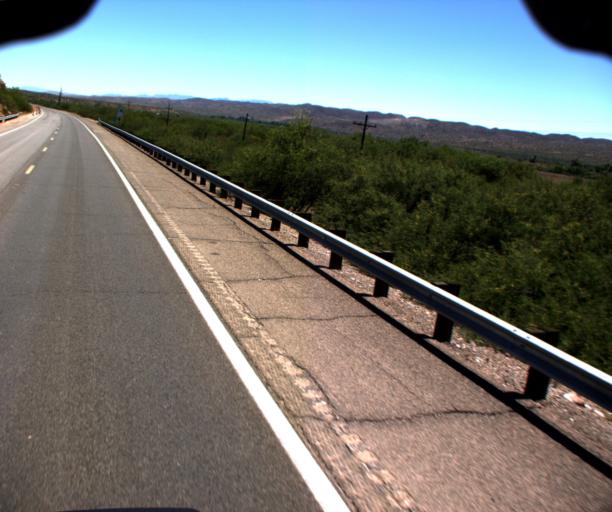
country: US
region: Arizona
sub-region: Pinal County
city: Mammoth
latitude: 32.8886
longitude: -110.7160
